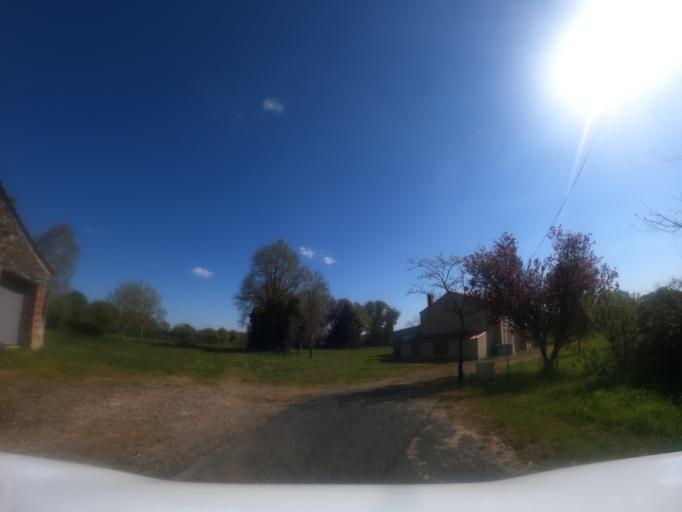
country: FR
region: Pays de la Loire
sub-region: Departement de la Vendee
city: Saint-Vincent-sur-Graon
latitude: 46.5241
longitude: -1.3756
